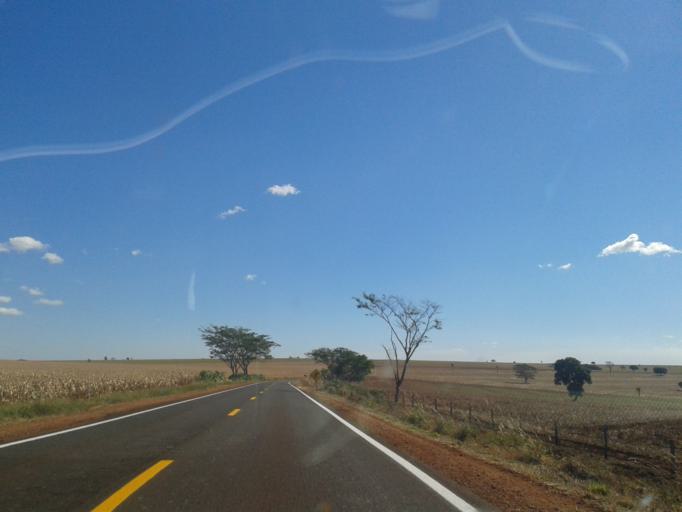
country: BR
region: Minas Gerais
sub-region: Capinopolis
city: Capinopolis
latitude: -18.6930
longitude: -49.4848
